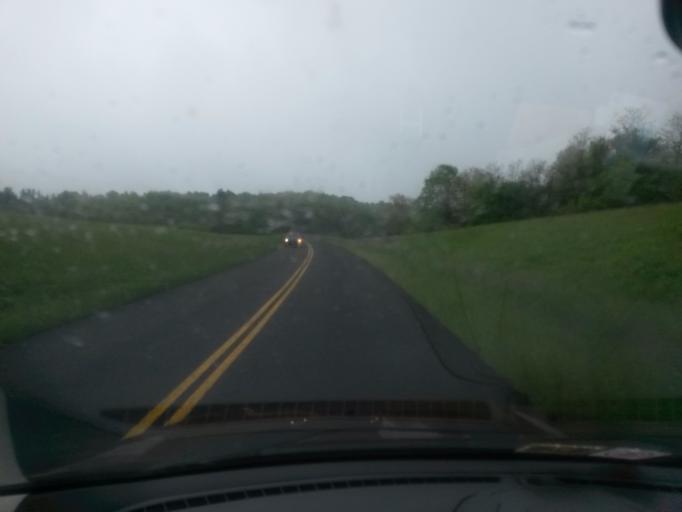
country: US
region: Virginia
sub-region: Floyd County
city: Floyd
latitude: 36.7970
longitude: -80.3869
